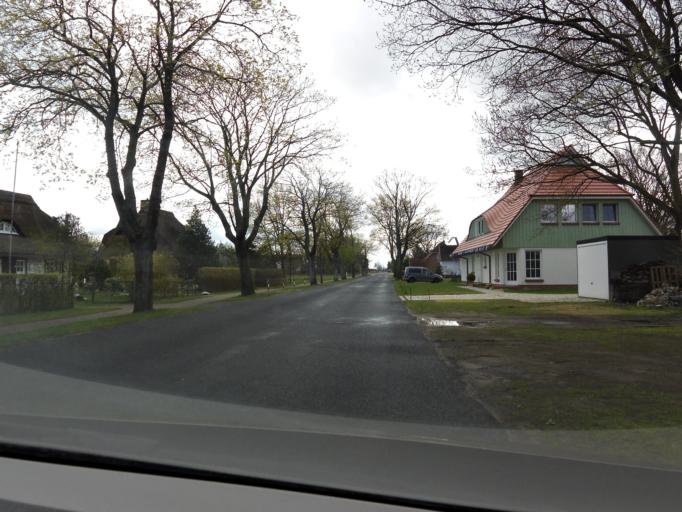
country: DE
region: Mecklenburg-Vorpommern
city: Ostseebad Prerow
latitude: 54.4123
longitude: 12.5816
